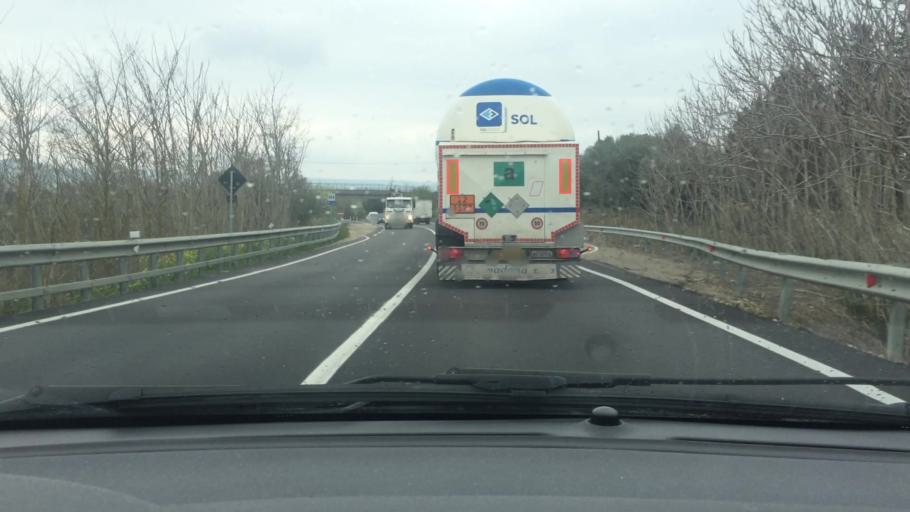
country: IT
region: Basilicate
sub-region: Provincia di Matera
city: Matera
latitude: 40.6161
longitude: 16.5789
